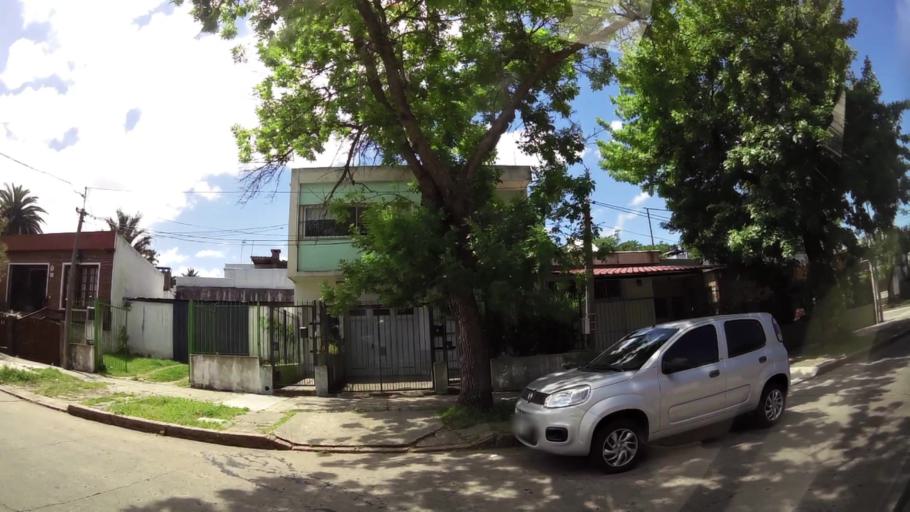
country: UY
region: Montevideo
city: Montevideo
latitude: -34.8616
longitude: -56.1879
